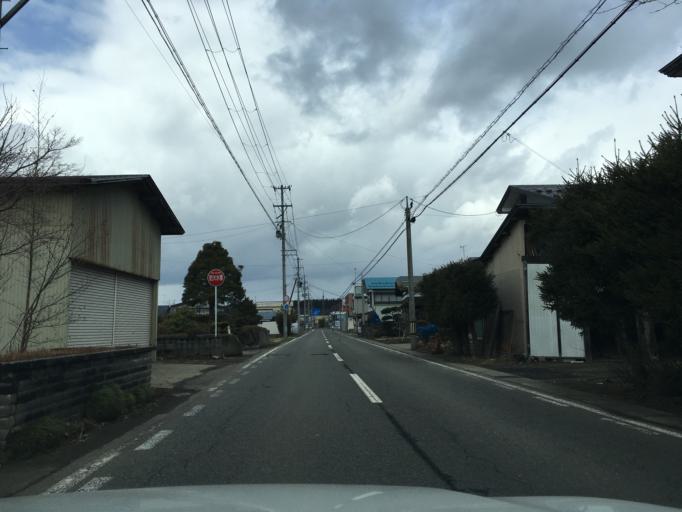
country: JP
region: Akita
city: Takanosu
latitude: 40.1560
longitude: 140.3347
